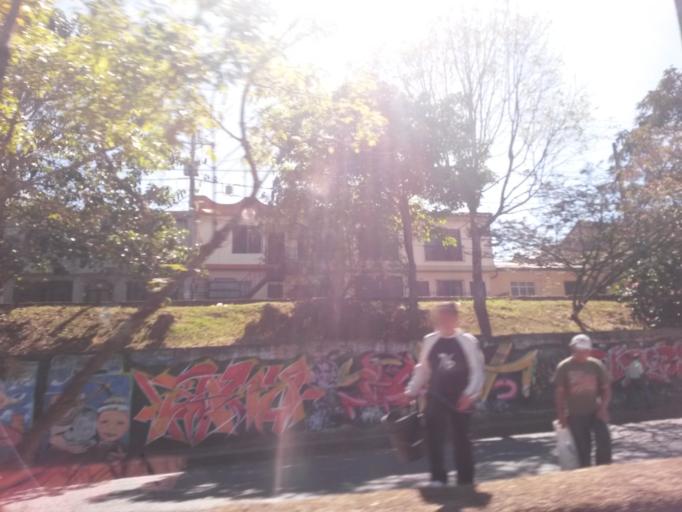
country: CO
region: Cauca
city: Popayan
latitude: 2.4496
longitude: -76.6247
